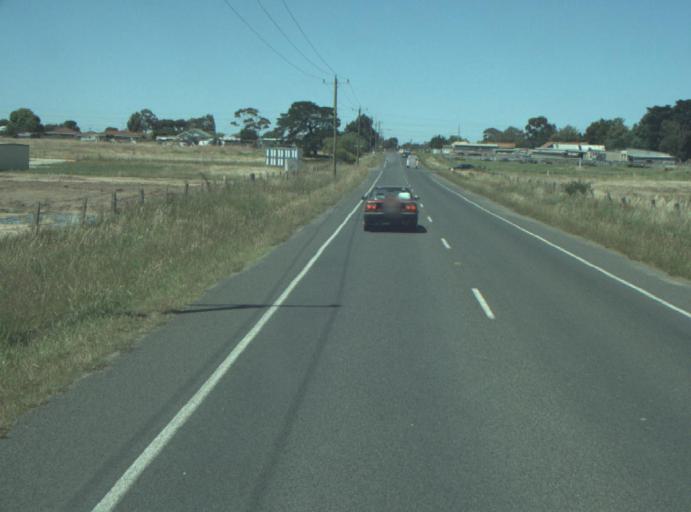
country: AU
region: Victoria
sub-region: Greater Geelong
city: Breakwater
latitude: -38.1933
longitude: 144.3532
